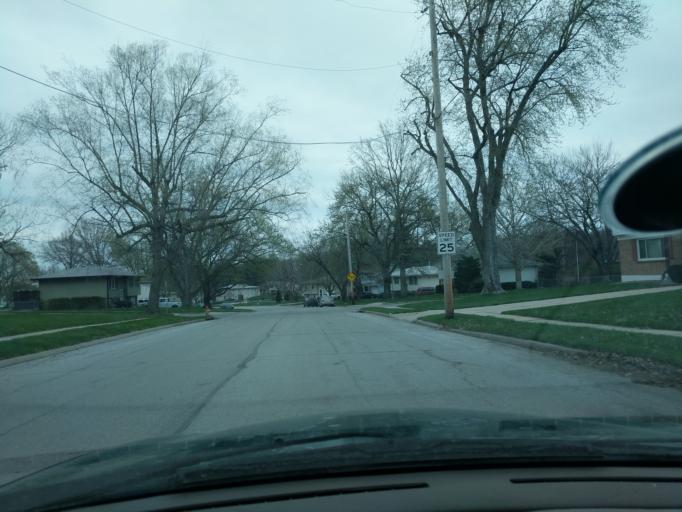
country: US
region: Nebraska
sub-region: Douglas County
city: Ralston
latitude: 41.2310
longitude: -96.0968
